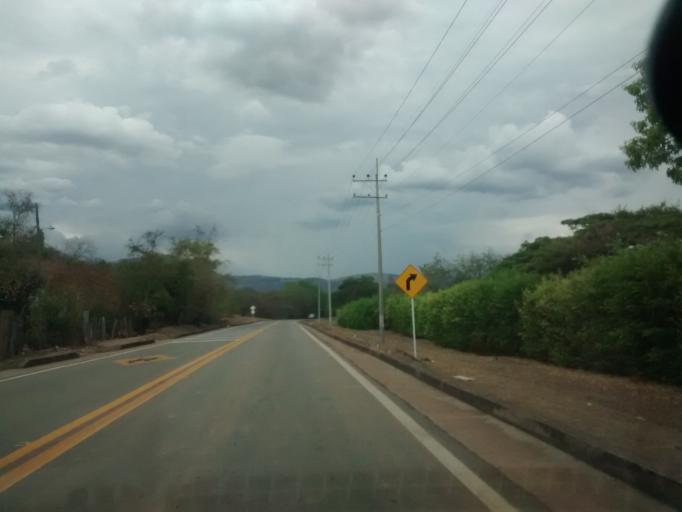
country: CO
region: Cundinamarca
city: Tocaima
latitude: 4.4400
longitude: -74.6774
